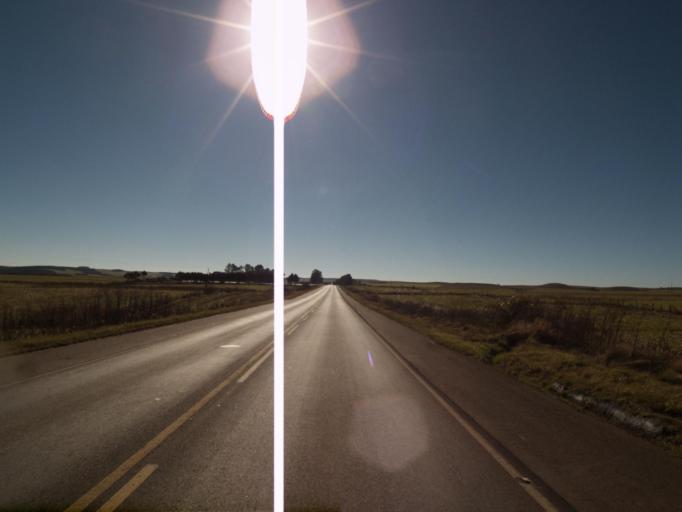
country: BR
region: Parana
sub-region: Palmas
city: Palmas
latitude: -26.7819
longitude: -51.6873
